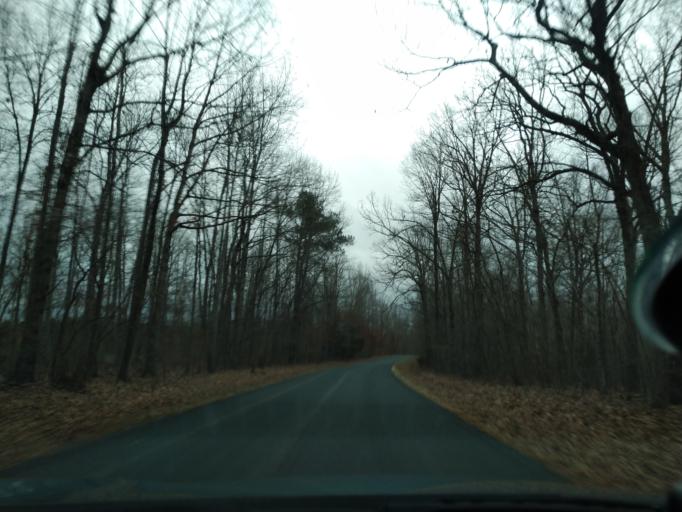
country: US
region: Virginia
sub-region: Appomattox County
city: Appomattox
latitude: 37.4070
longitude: -78.6684
